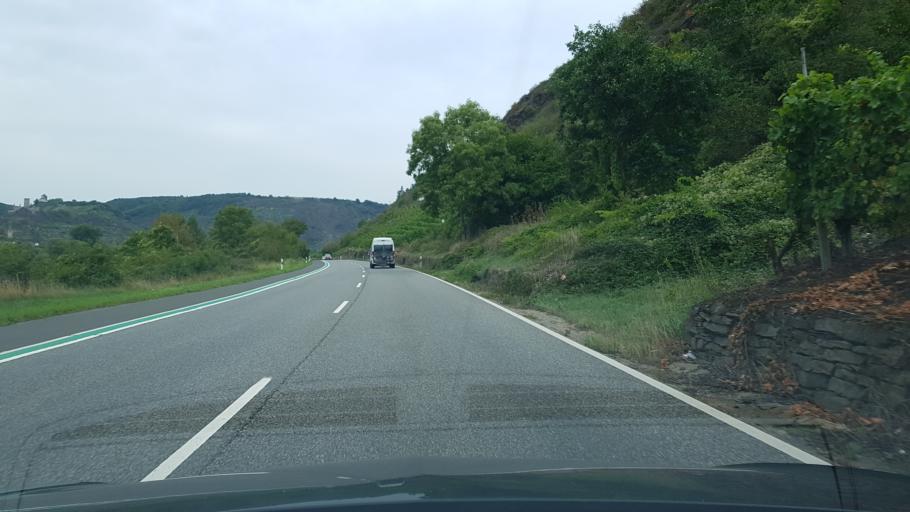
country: DE
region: Rheinland-Pfalz
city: Kobern-Gondorf
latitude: 50.2983
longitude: 7.4648
